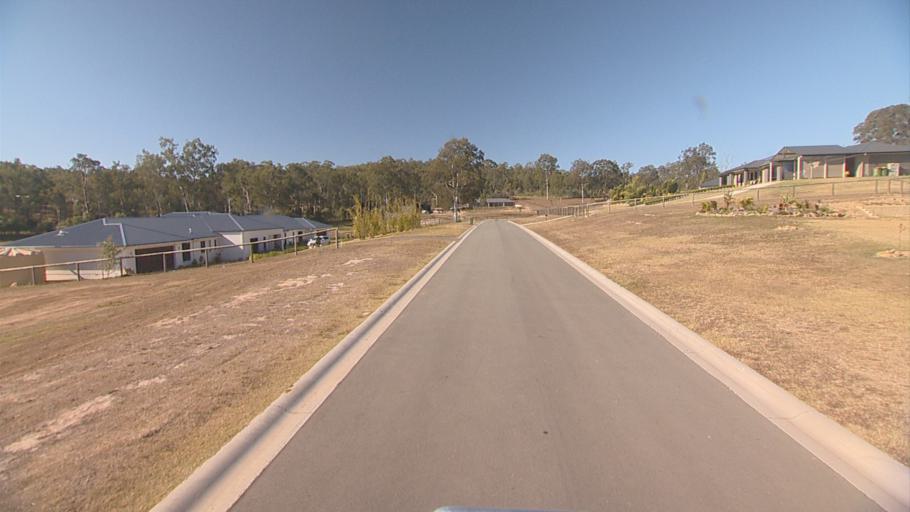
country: AU
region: Queensland
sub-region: Logan
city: Cedar Vale
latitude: -27.8680
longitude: 153.0593
